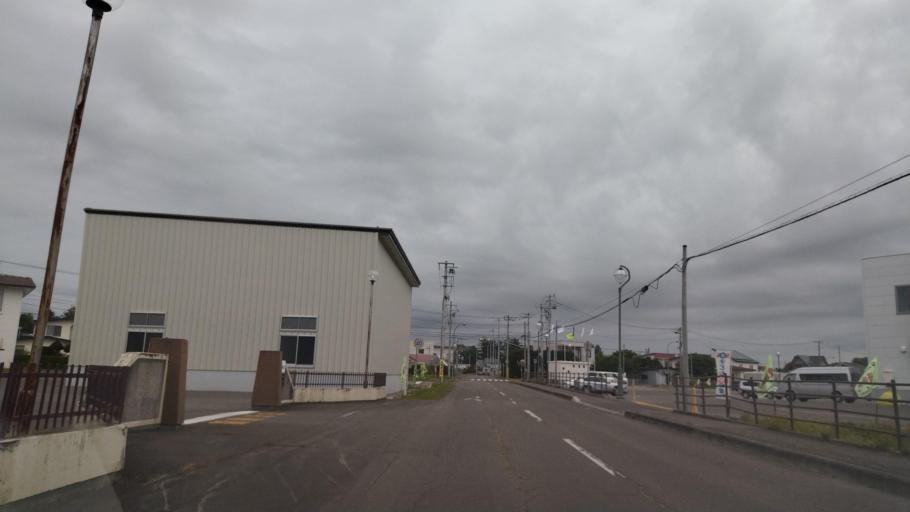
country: JP
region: Hokkaido
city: Otofuke
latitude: 43.2250
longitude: 143.2869
